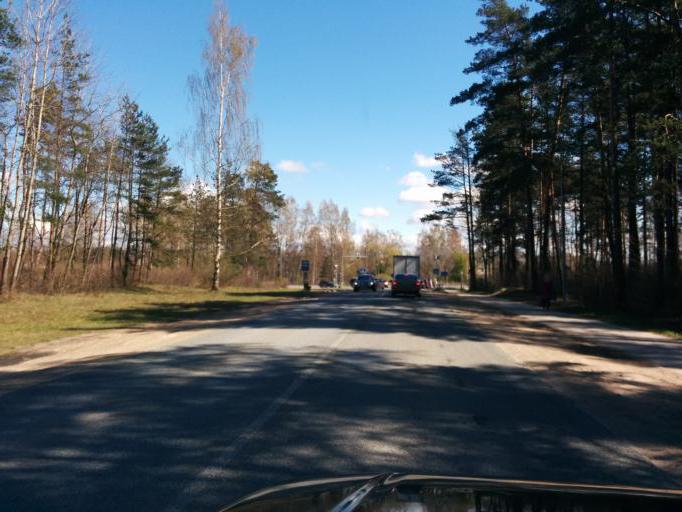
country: LV
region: Kekava
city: Balozi
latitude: 56.8843
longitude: 24.1527
